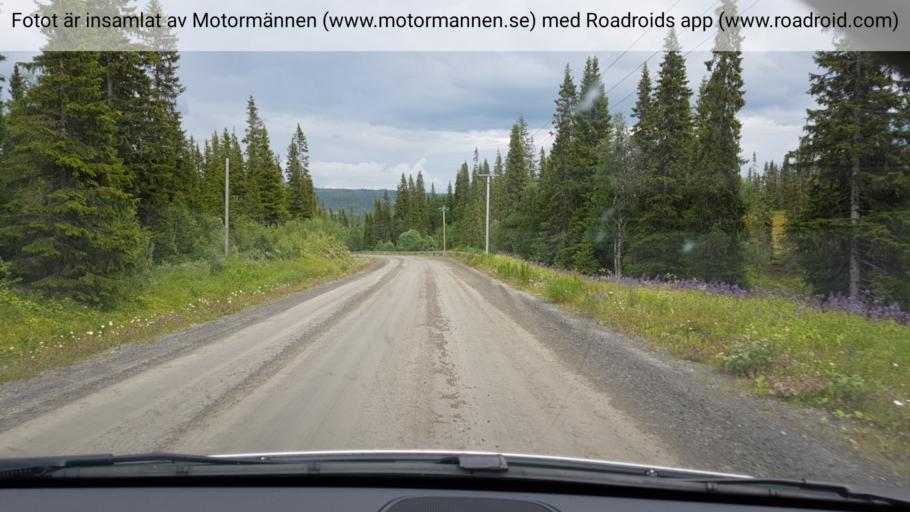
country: SE
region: Jaemtland
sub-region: Are Kommun
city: Are
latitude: 63.7033
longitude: 12.7182
